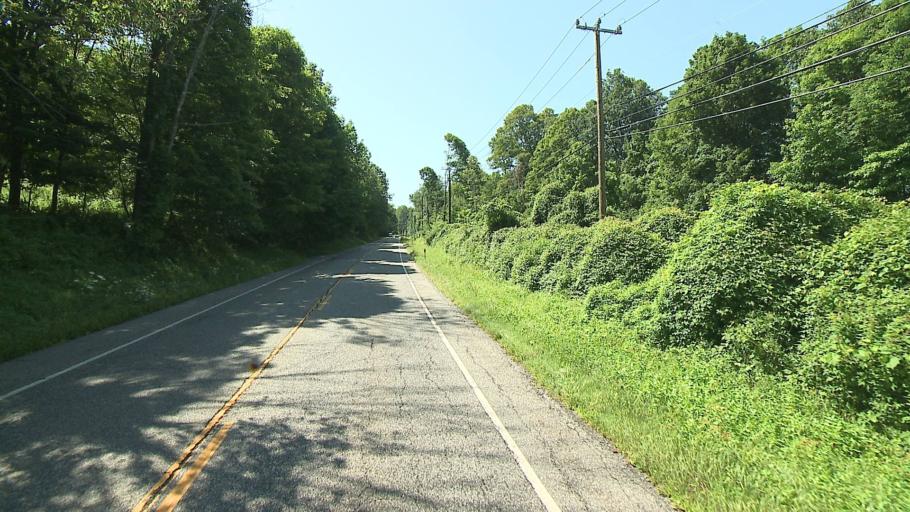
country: US
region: Connecticut
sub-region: Litchfield County
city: Kent
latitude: 41.8497
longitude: -73.4411
